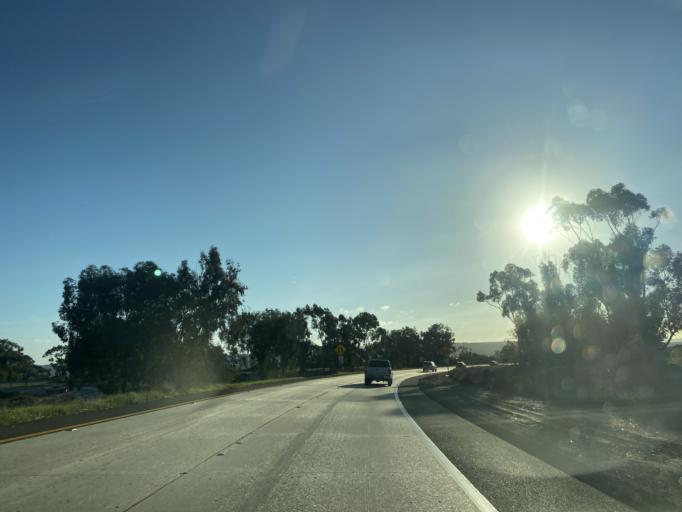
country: US
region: California
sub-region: San Diego County
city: Imperial Beach
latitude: 32.5699
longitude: -117.0416
